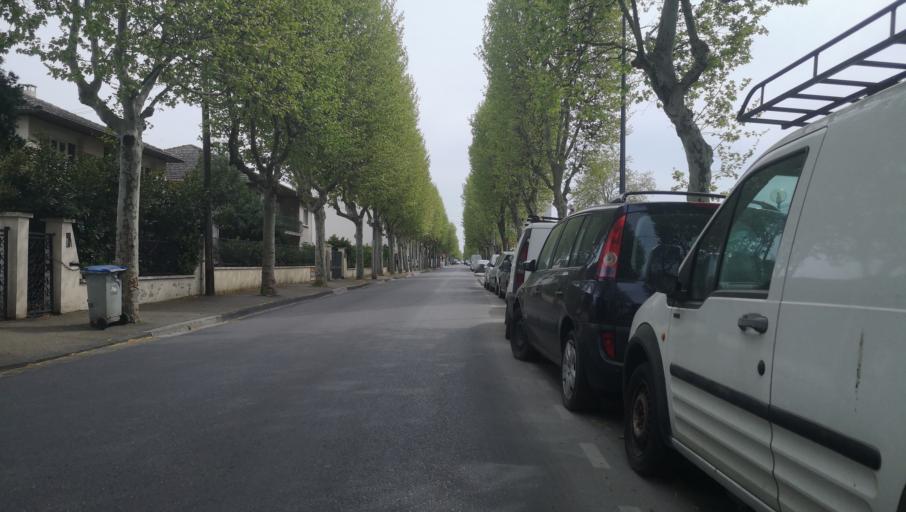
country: FR
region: Rhone-Alpes
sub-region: Departement du Rhone
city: Bron
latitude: 45.7553
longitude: 4.9283
